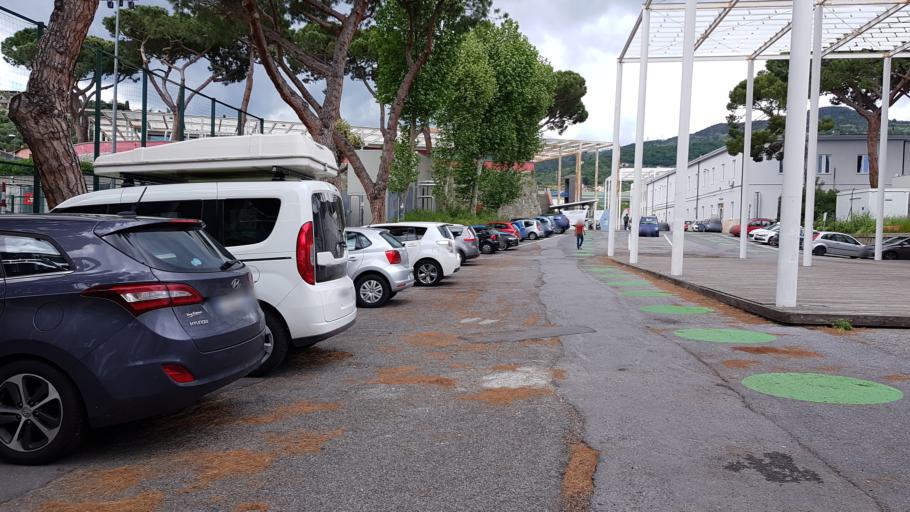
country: IT
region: Liguria
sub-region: Provincia di Savona
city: Savona
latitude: 44.2997
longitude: 8.4514
